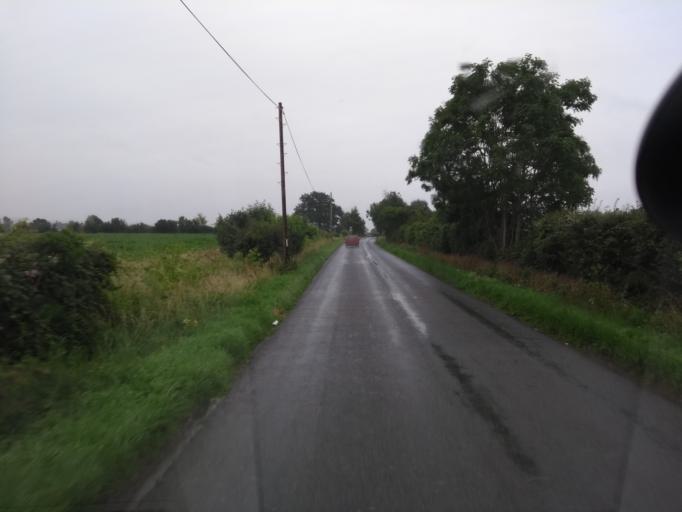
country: GB
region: England
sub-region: Somerset
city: Ilchester
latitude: 51.0720
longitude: -2.6842
